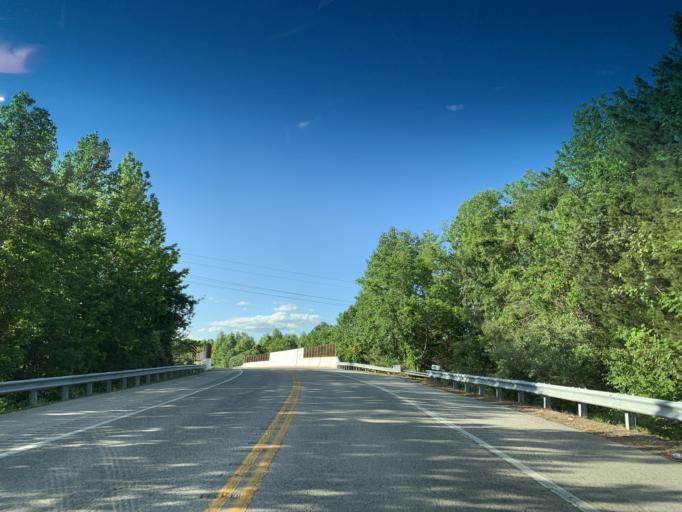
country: US
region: Maryland
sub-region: Cecil County
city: Elkton
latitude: 39.6020
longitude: -75.8601
